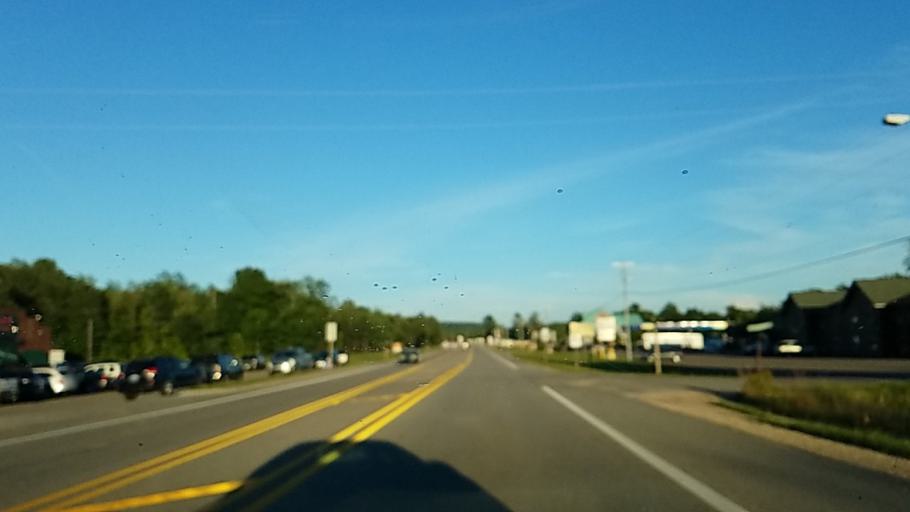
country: US
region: Michigan
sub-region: Alger County
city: Munising
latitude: 46.4386
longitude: -86.7107
